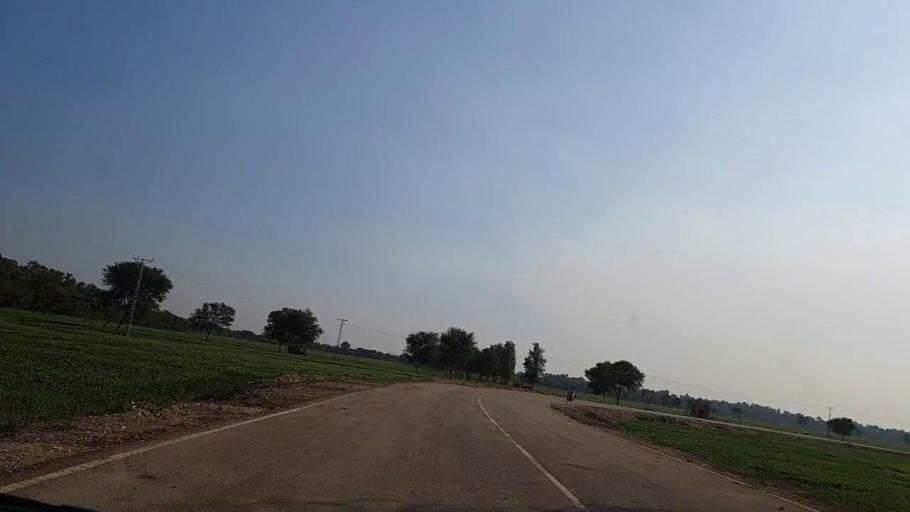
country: PK
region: Sindh
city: Sakrand
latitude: 26.1187
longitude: 68.2496
